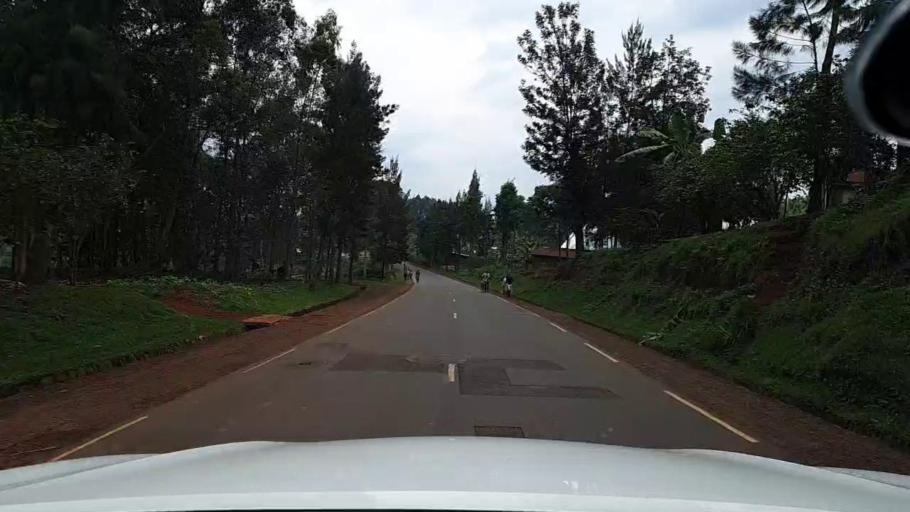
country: RW
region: Western Province
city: Cyangugu
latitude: -2.6111
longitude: 28.9370
